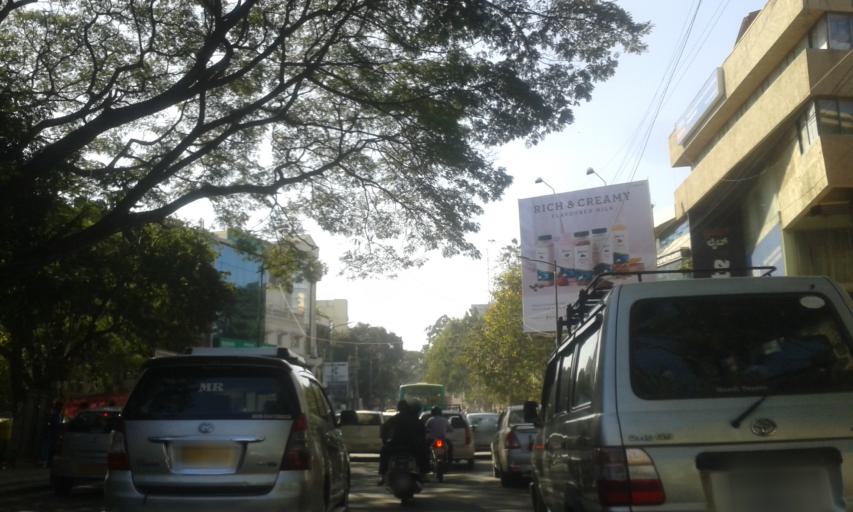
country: IN
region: Karnataka
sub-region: Bangalore Urban
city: Bangalore
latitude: 12.9656
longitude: 77.6030
